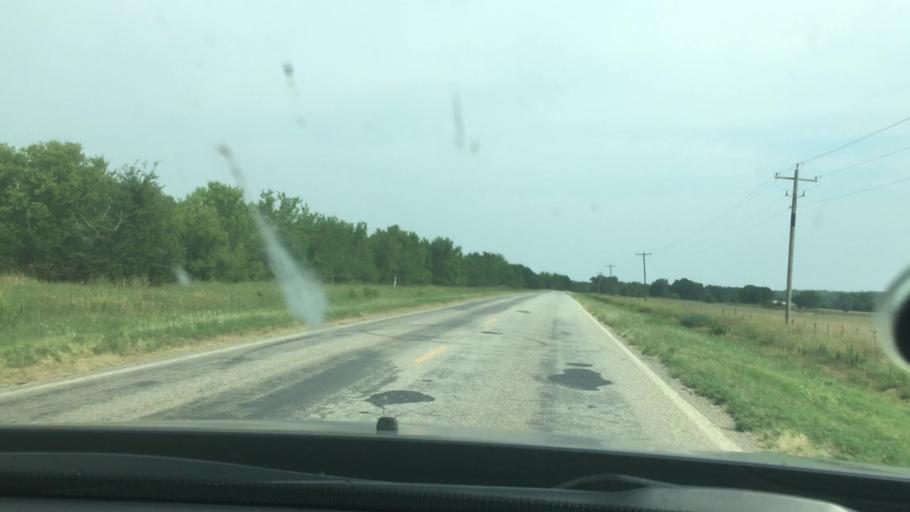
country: US
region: Oklahoma
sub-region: Johnston County
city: Tishomingo
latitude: 34.3467
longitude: -96.4233
